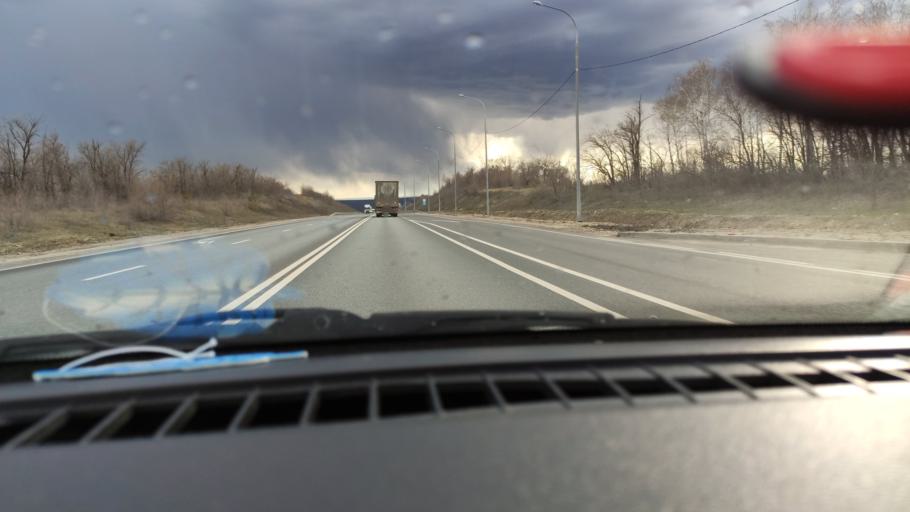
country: RU
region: Saratov
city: Yelshanka
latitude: 51.8891
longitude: 46.5211
